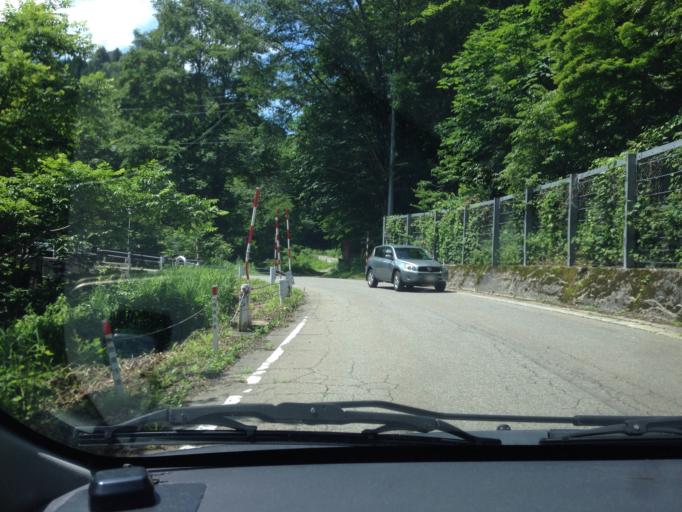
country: JP
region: Fukushima
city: Kitakata
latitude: 37.2568
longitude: 139.7288
